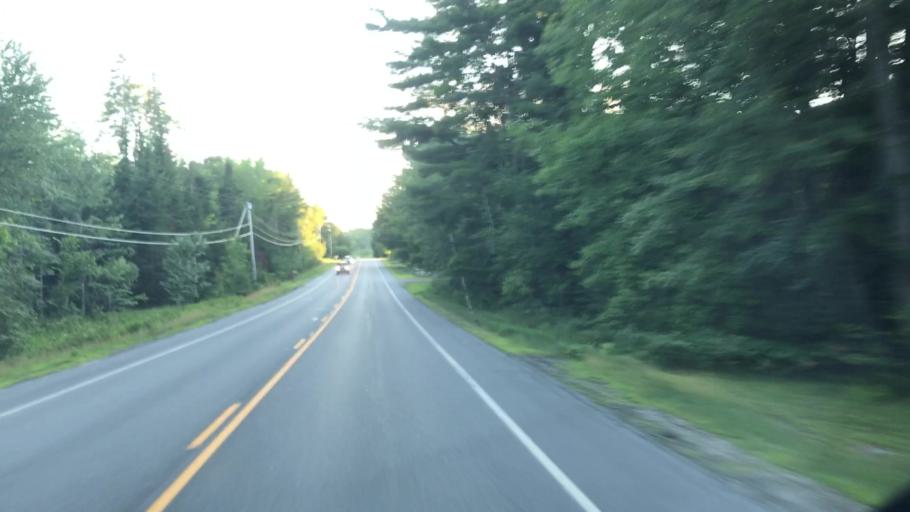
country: US
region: Maine
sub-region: Penobscot County
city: Lincoln
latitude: 45.3782
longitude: -68.4556
